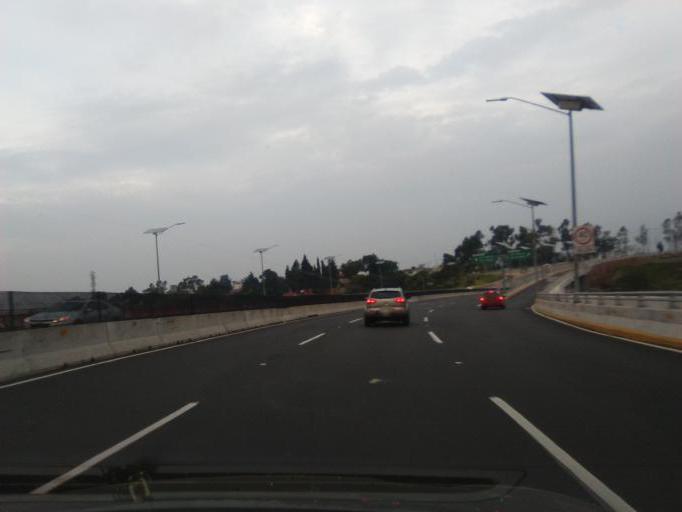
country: MX
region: Mexico City
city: Magdalena Contreras
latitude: 19.3465
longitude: -99.2415
